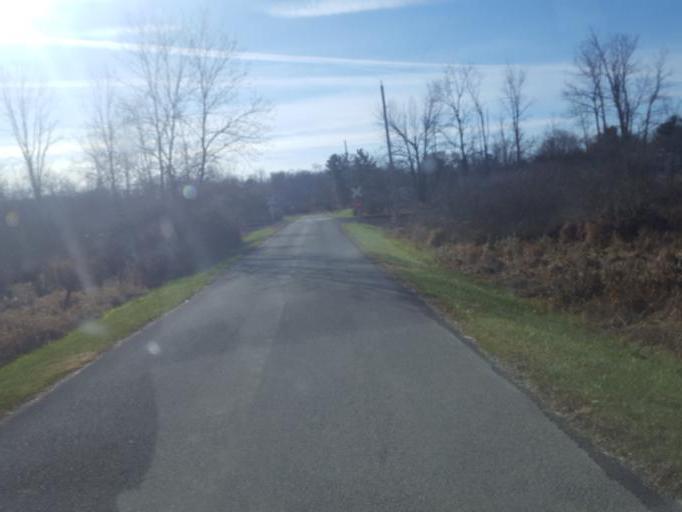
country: US
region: Ohio
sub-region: Richland County
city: Ontario
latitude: 40.8157
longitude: -82.5870
